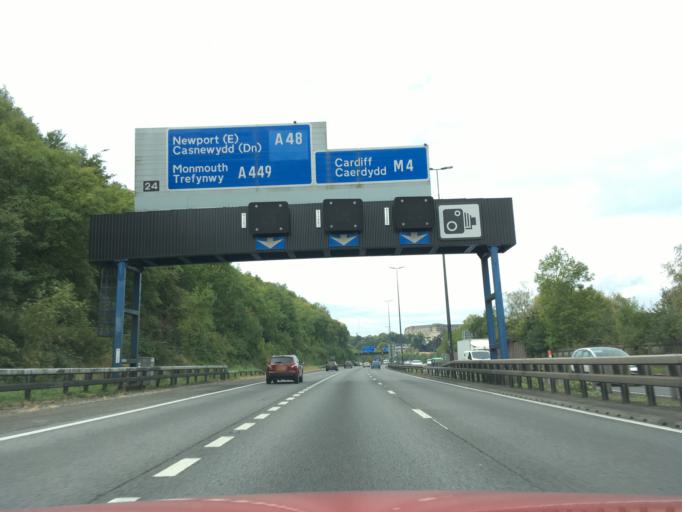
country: GB
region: Wales
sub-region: Newport
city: Langstone
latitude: 51.6015
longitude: -2.9158
